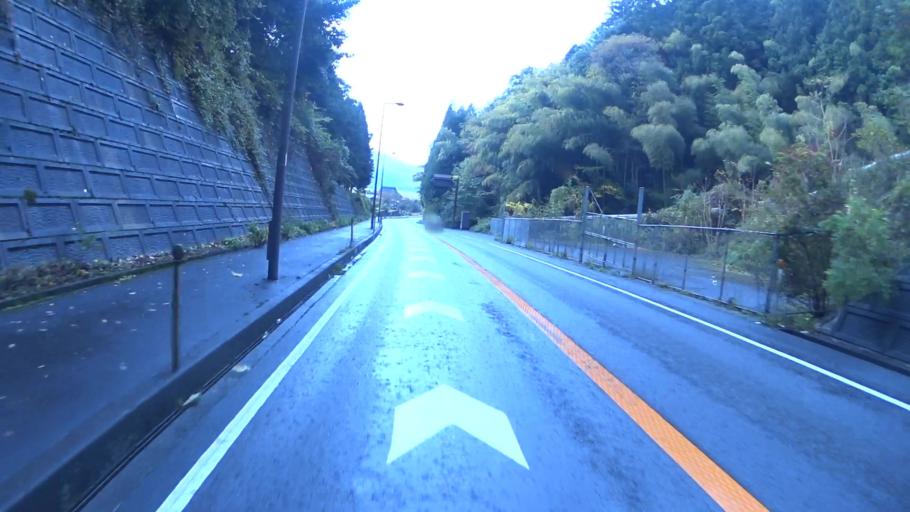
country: JP
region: Kyoto
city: Fukuchiyama
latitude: 35.3962
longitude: 135.1571
